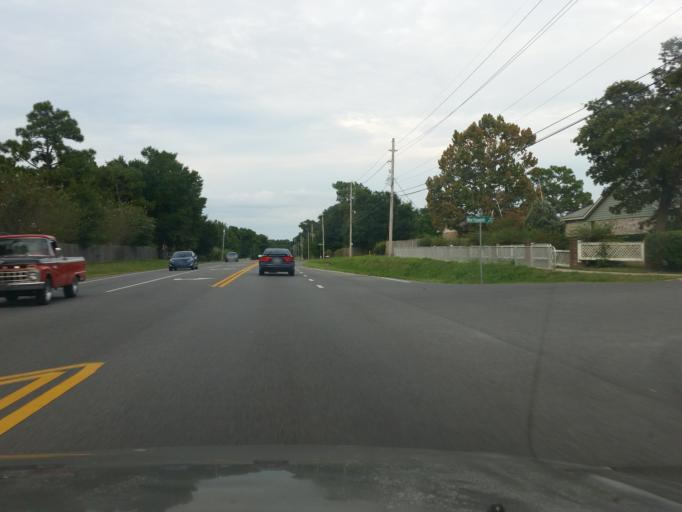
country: US
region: Florida
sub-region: Escambia County
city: Ferry Pass
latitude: 30.5130
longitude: -87.1824
